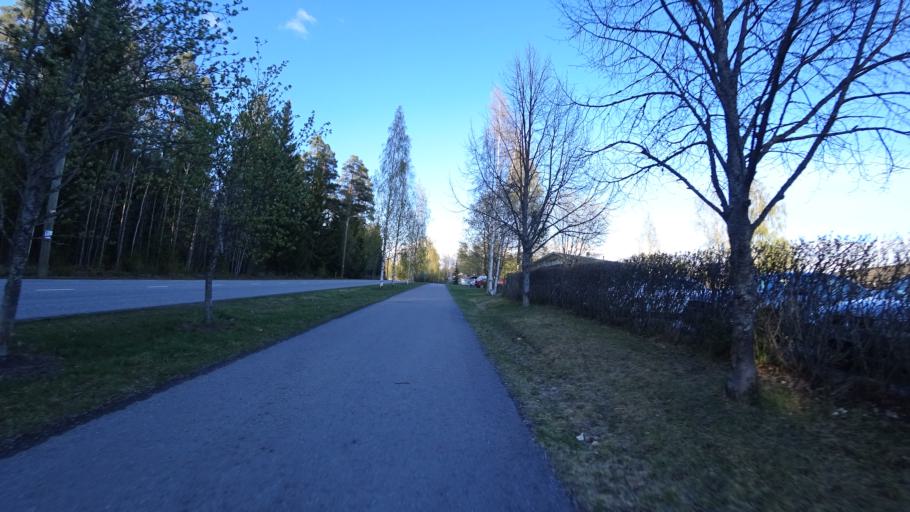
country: FI
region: Pirkanmaa
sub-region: Tampere
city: Nokia
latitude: 61.4911
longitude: 23.5521
